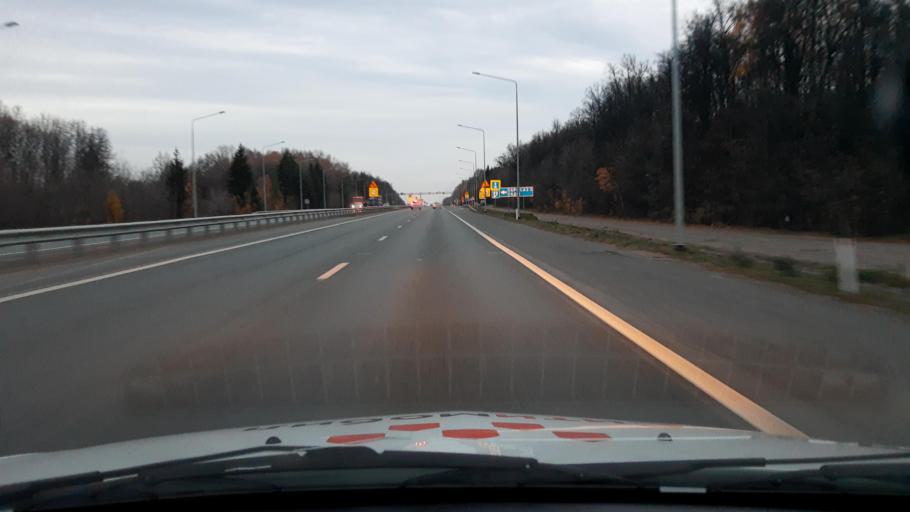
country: RU
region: Bashkortostan
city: Kabakovo
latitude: 54.4320
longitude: 55.9214
